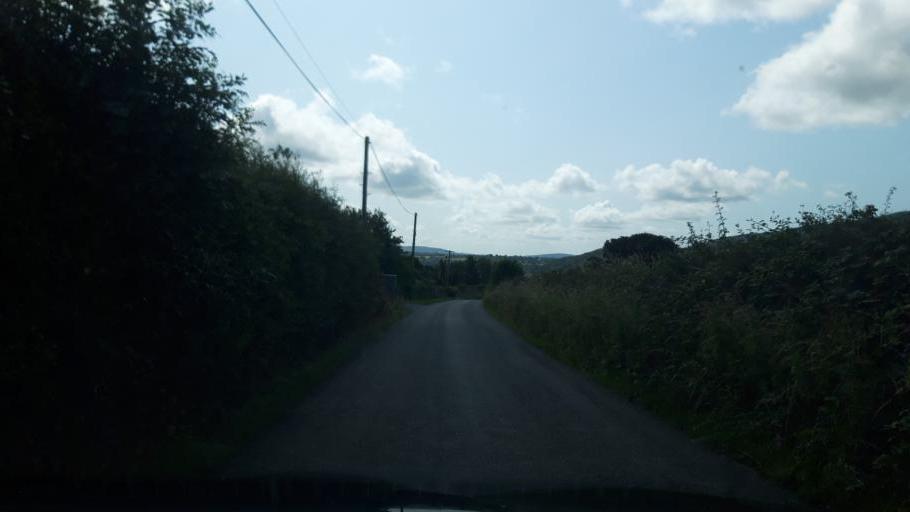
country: IE
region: Leinster
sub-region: Kilkenny
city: Graiguenamanagh
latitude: 52.5490
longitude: -6.9698
